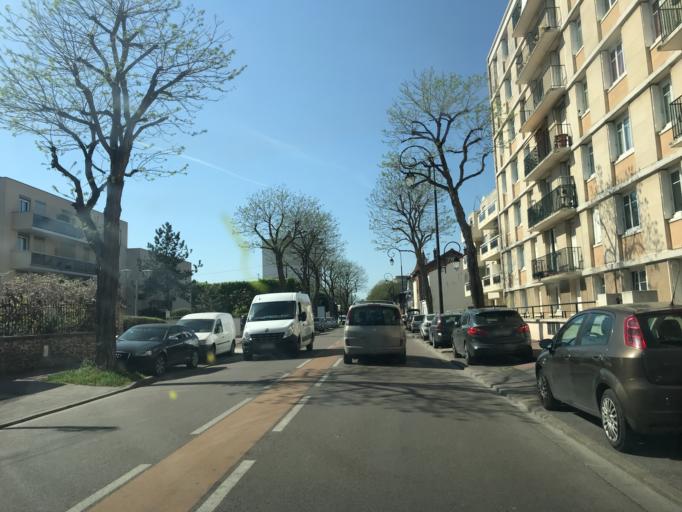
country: FR
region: Ile-de-France
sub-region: Departement du Val-de-Marne
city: Saint-Maur-des-Fosses
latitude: 48.8007
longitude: 2.4959
